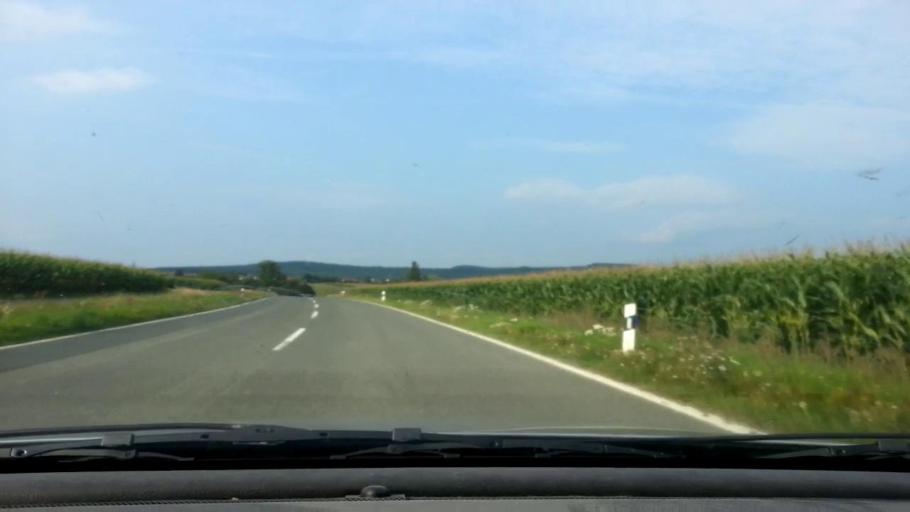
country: DE
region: Bavaria
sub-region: Upper Franconia
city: Litzendorf
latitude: 49.9014
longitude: 11.0103
